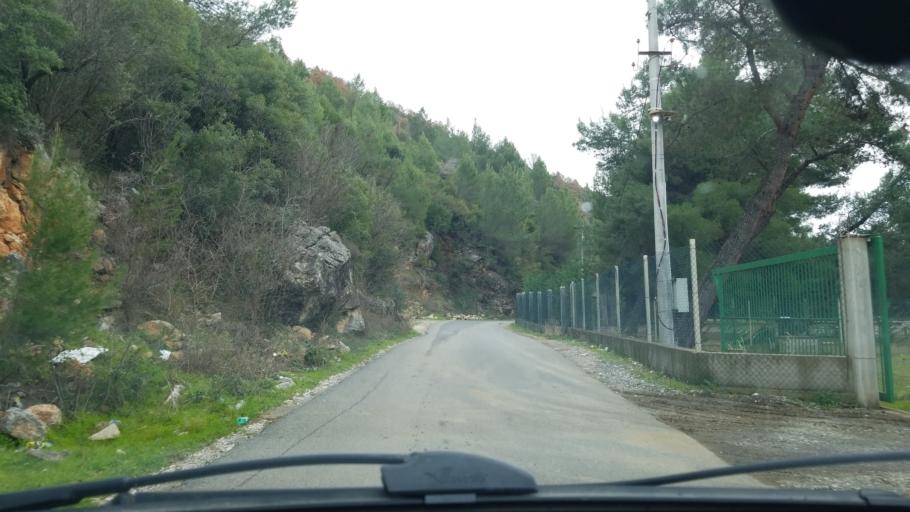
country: AL
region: Lezhe
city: Shengjin
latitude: 41.8203
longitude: 19.5638
